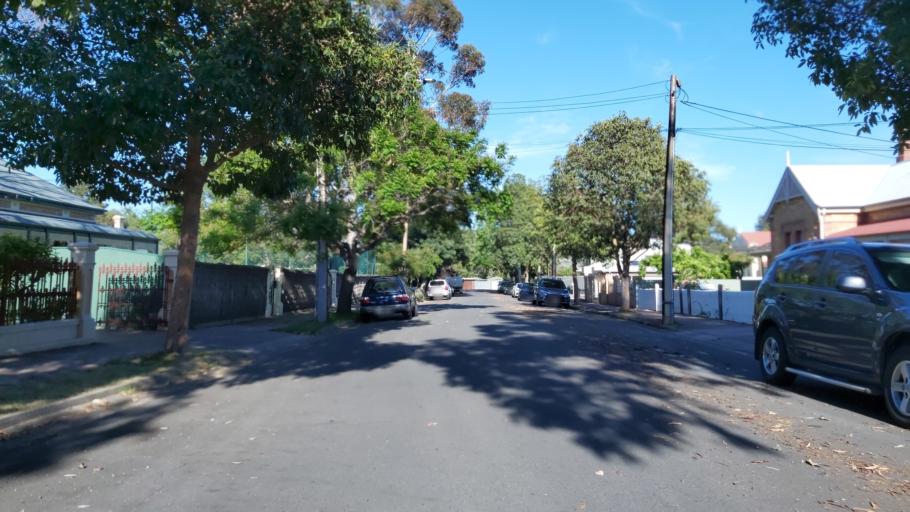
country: AU
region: South Australia
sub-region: Unley
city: Fullarton
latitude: -34.9505
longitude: 138.6176
